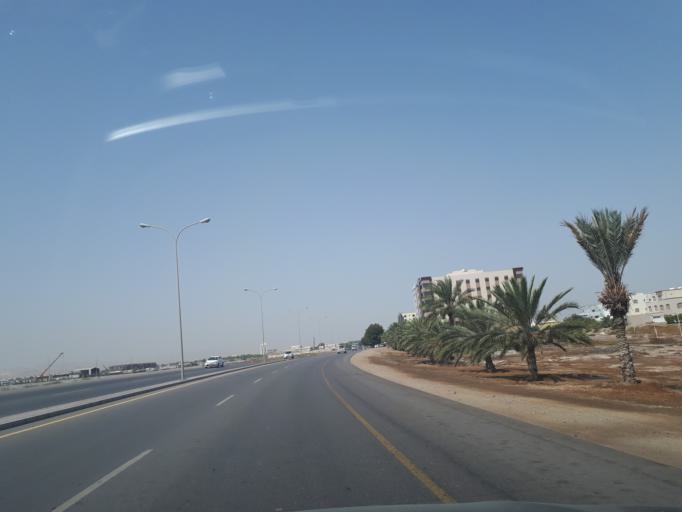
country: OM
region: Muhafazat Masqat
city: As Sib al Jadidah
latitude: 23.6209
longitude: 58.2610
